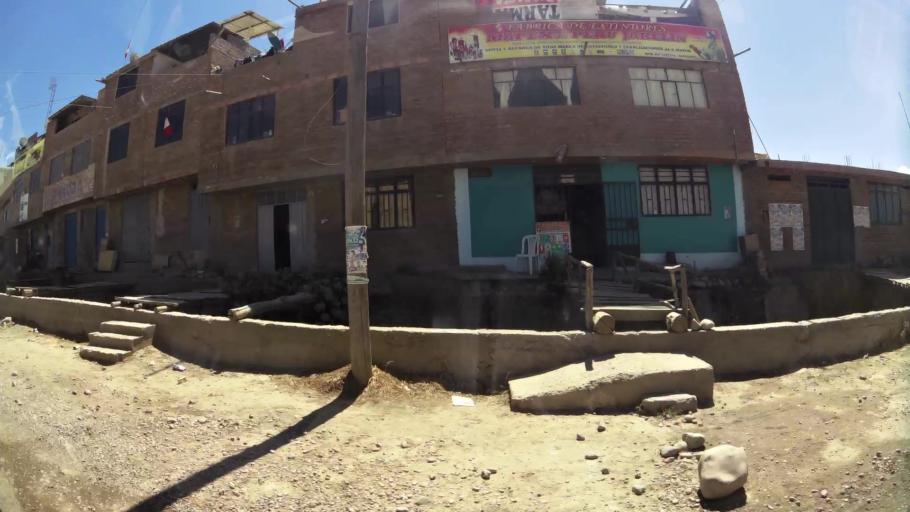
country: PE
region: Junin
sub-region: Provincia de Jauja
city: Jauja
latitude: -11.7776
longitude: -75.4936
